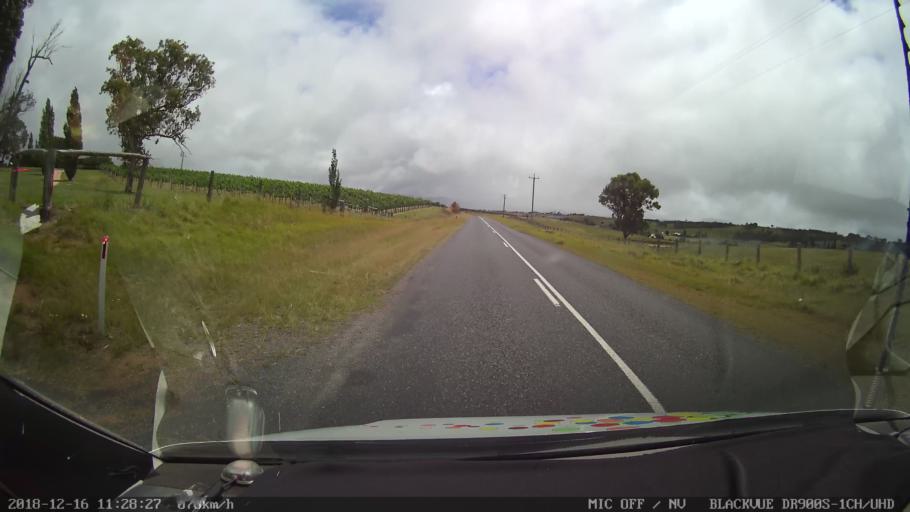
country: AU
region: New South Wales
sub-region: Tenterfield Municipality
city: Carrolls Creek
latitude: -29.0392
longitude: 152.0979
